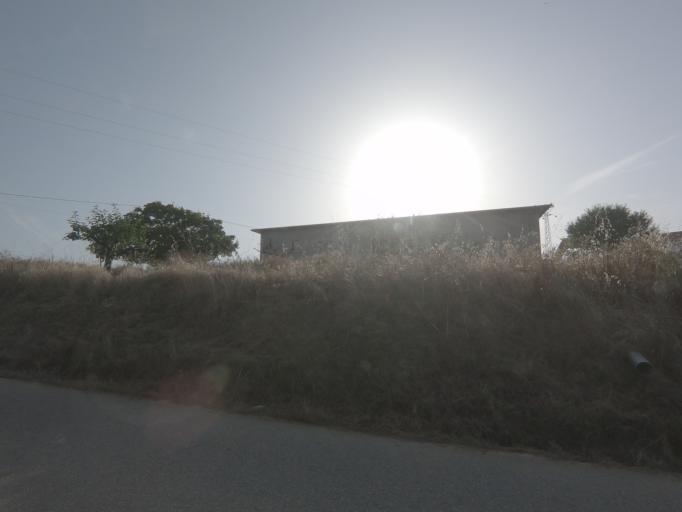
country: PT
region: Vila Real
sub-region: Sabrosa
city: Sabrosa
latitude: 41.2561
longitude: -7.4659
